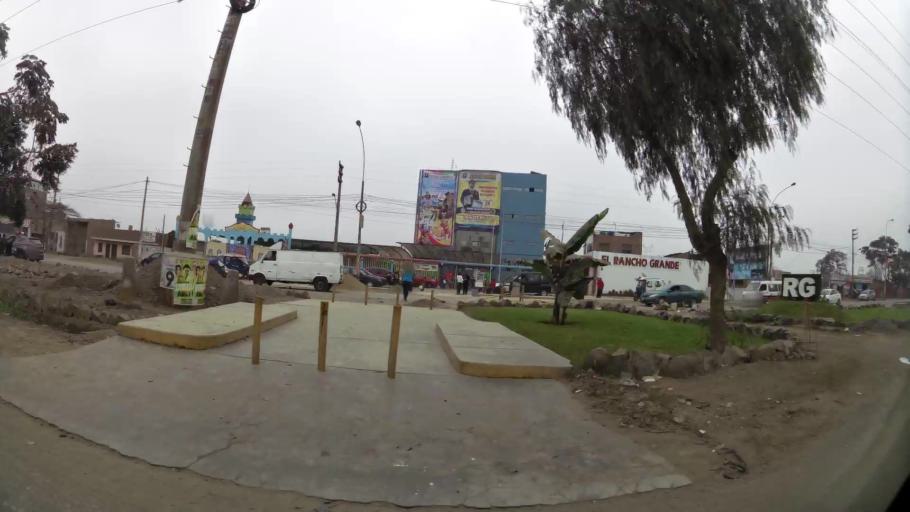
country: PE
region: Lima
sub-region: Lima
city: Urb. Santo Domingo
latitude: -11.8991
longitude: -77.0496
